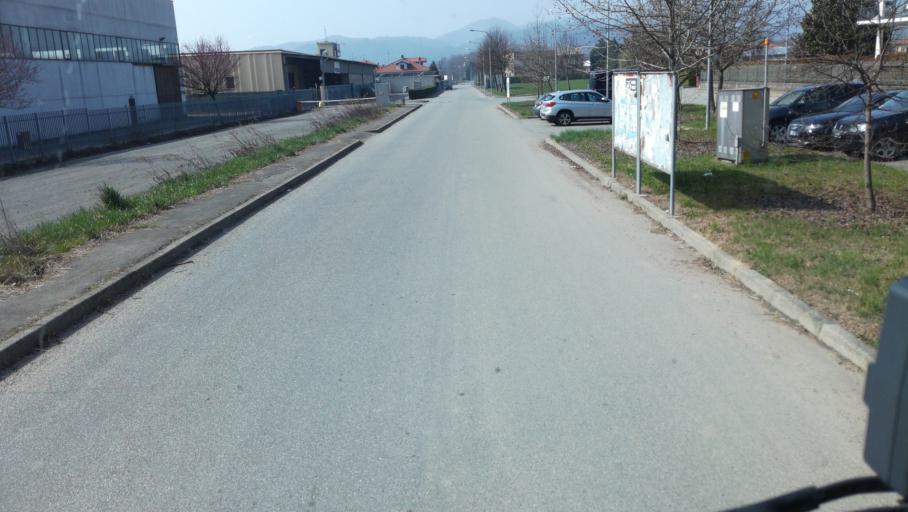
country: IT
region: Piedmont
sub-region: Provincia di Novara
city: Grignasco
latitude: 45.6724
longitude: 8.3544
